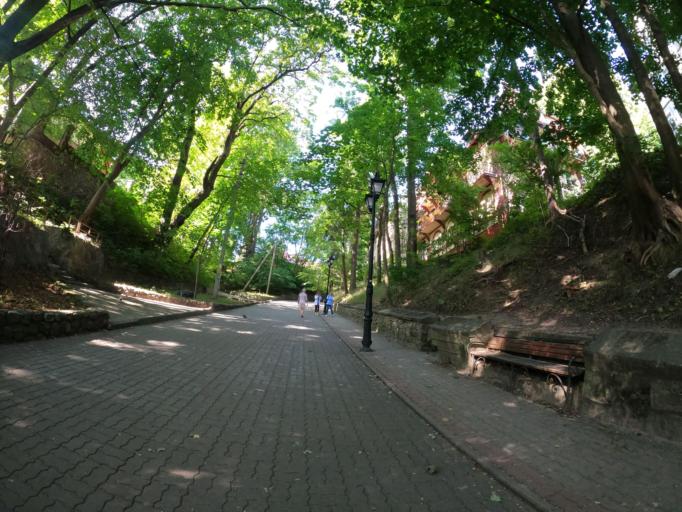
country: RU
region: Kaliningrad
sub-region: Gorod Svetlogorsk
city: Svetlogorsk
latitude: 54.9391
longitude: 20.1564
